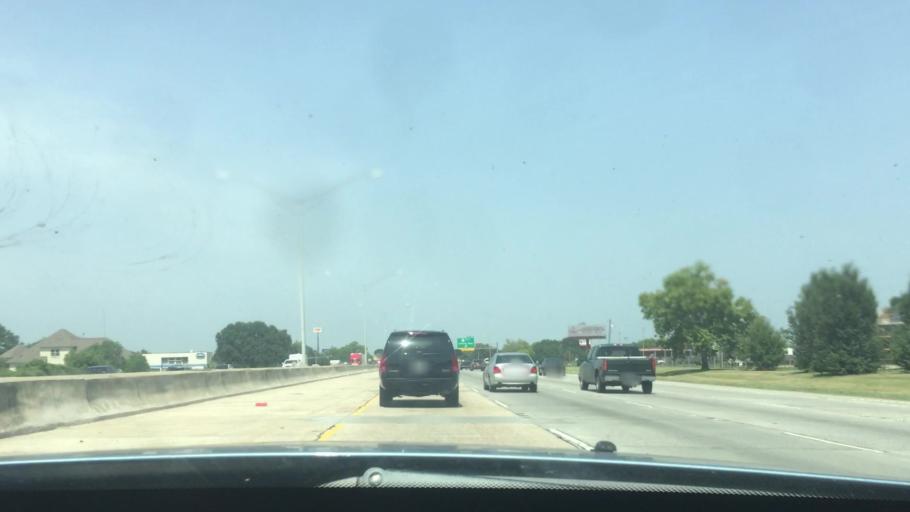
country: US
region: Louisiana
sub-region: East Baton Rouge Parish
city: Westminster
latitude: 30.4209
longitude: -91.0817
